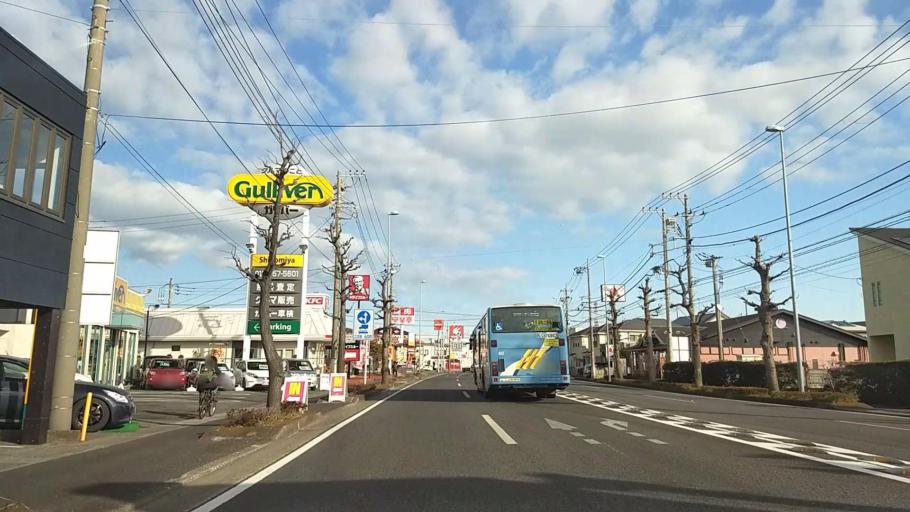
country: JP
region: Kanagawa
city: Hiratsuka
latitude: 35.3583
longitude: 139.3582
